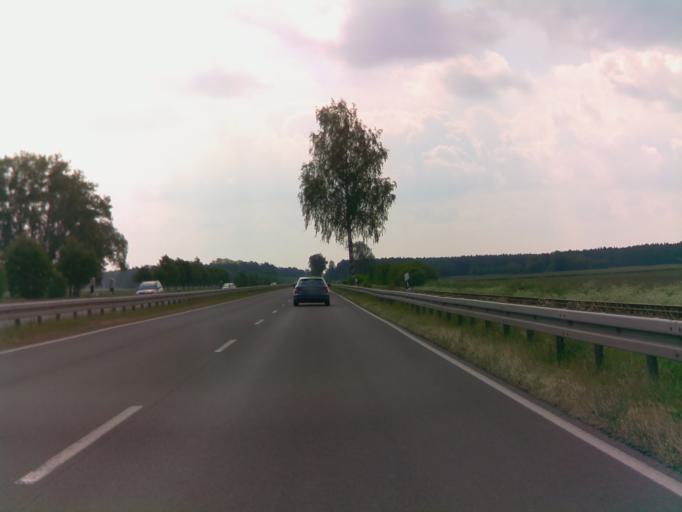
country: DE
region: Saxony-Anhalt
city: Stendal
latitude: 52.5770
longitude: 11.9122
